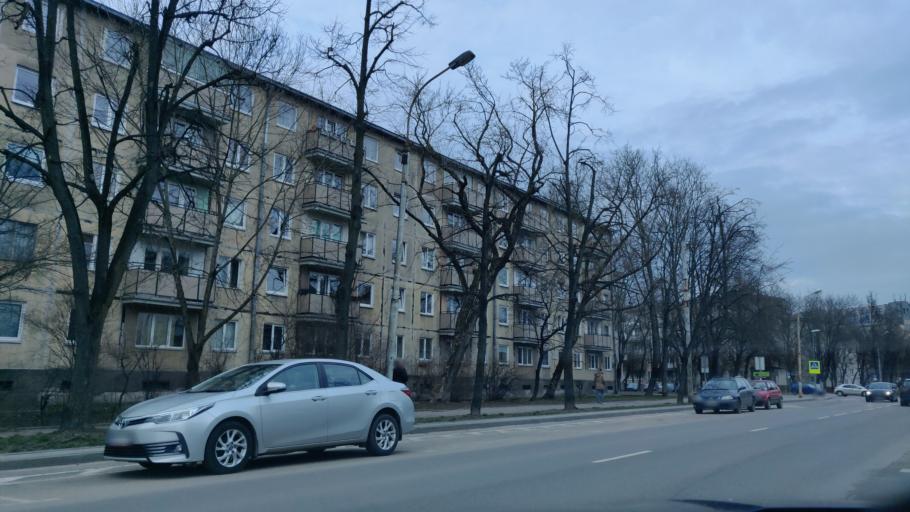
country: LT
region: Vilnius County
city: Naujamiestis
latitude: 54.6714
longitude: 25.2618
